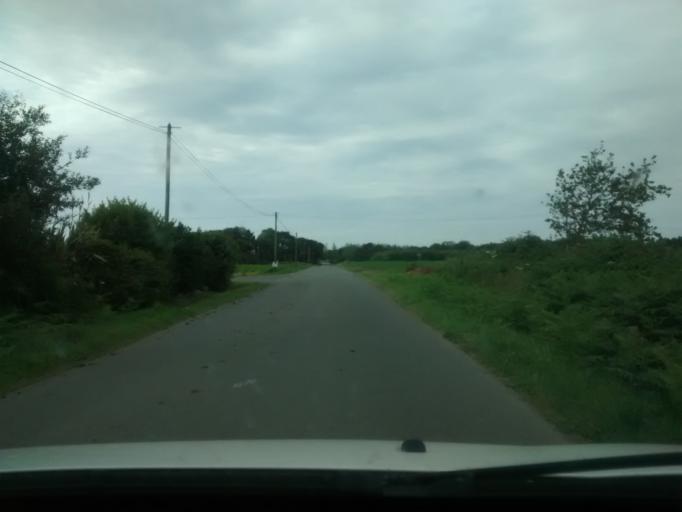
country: FR
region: Brittany
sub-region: Departement des Cotes-d'Armor
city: Trelevern
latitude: 48.7952
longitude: -3.3631
